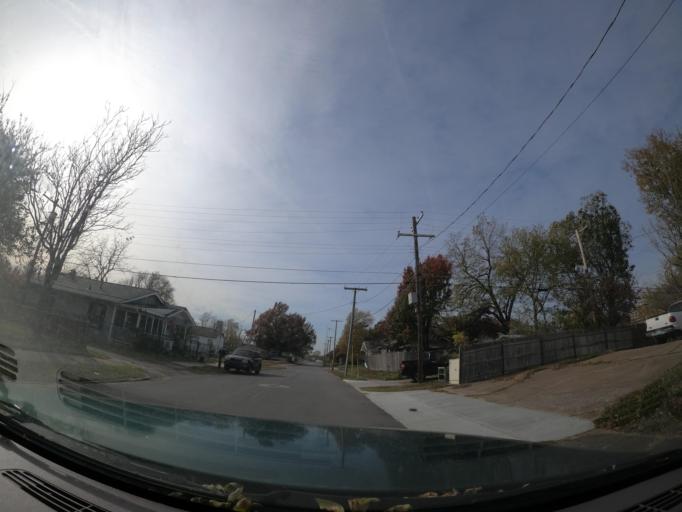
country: US
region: Oklahoma
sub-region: Tulsa County
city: Tulsa
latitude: 36.1626
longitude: -95.9651
